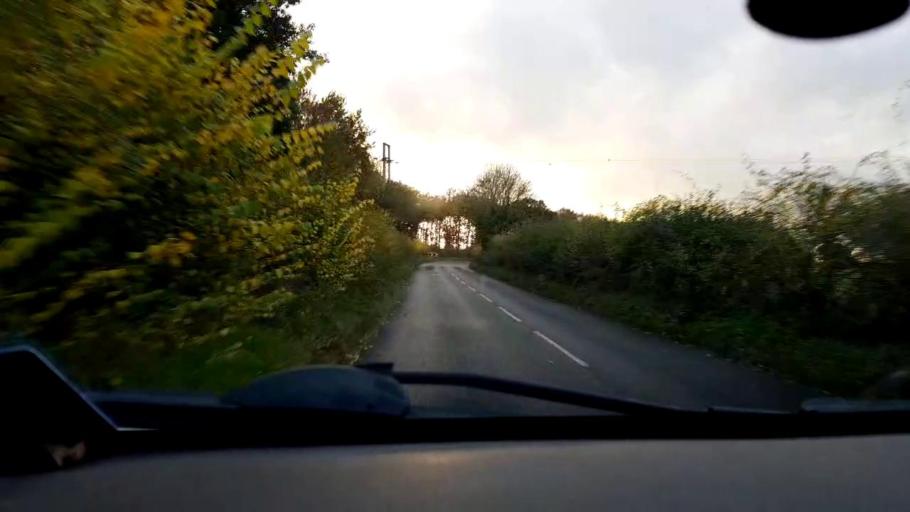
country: GB
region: England
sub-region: Norfolk
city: Spixworth
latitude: 52.6908
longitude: 1.3052
